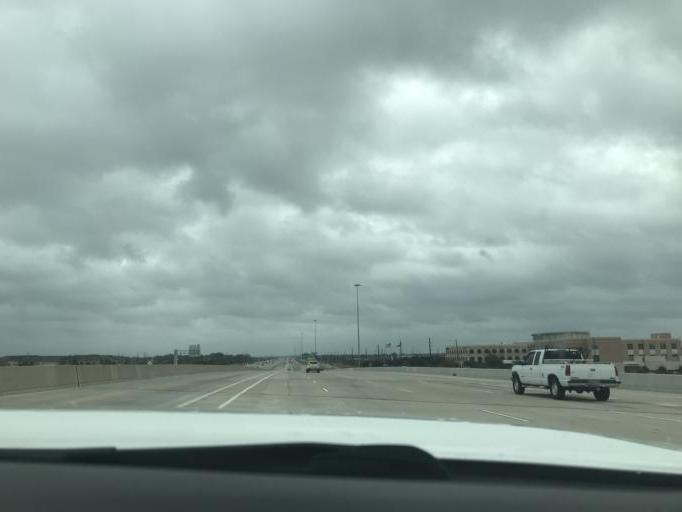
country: US
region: Texas
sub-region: Fort Bend County
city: Greatwood
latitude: 29.5559
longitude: -95.7168
